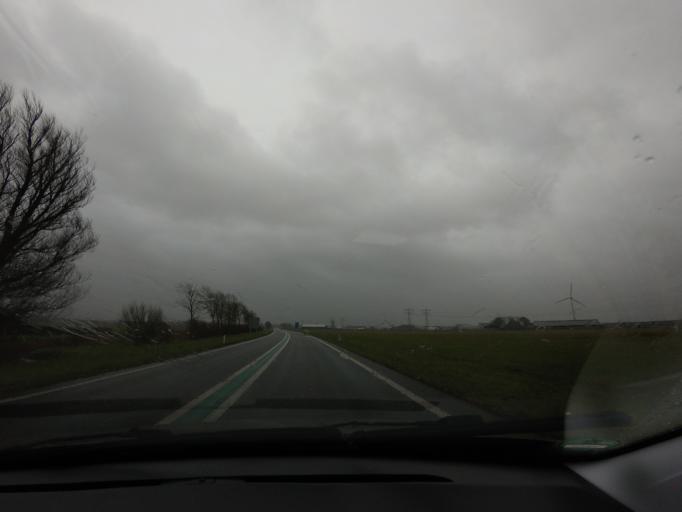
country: NL
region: Friesland
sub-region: Sudwest Fryslan
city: Bolsward
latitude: 53.0733
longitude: 5.5110
